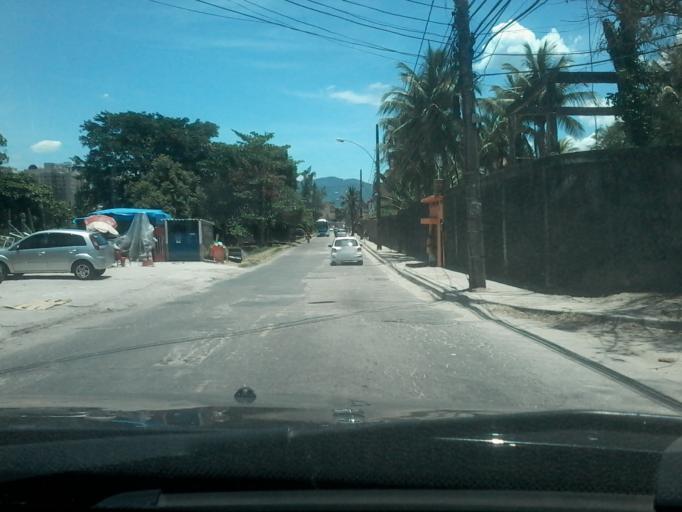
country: BR
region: Rio de Janeiro
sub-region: Nilopolis
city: Nilopolis
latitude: -23.0290
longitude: -43.4803
